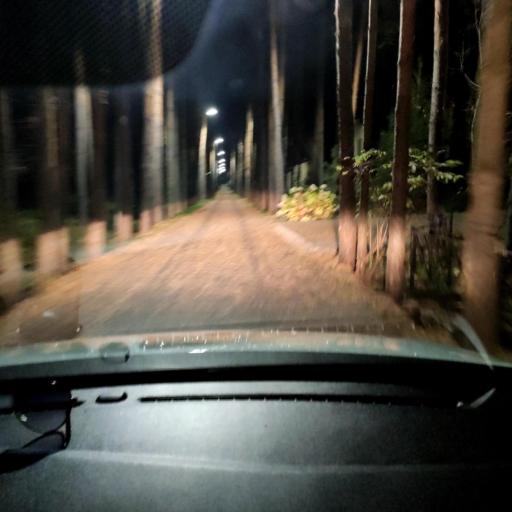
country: RU
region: Tatarstan
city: Verkhniy Uslon
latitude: 55.6207
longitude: 49.0206
